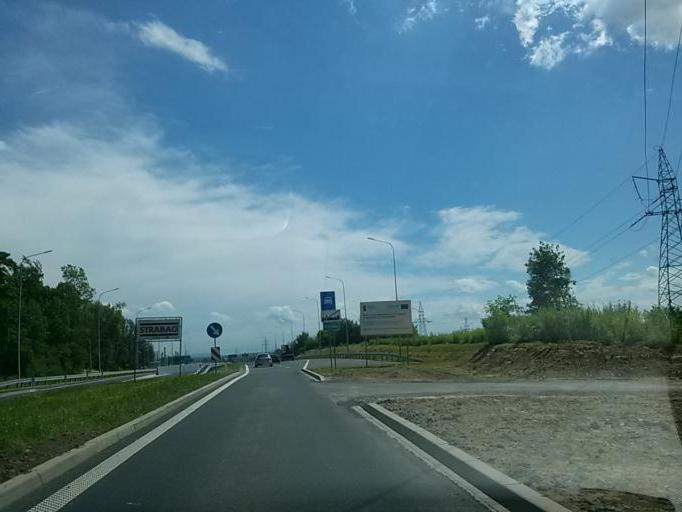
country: PL
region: Lesser Poland Voivodeship
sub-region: Powiat wielicki
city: Kokotow
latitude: 50.0712
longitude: 20.0651
